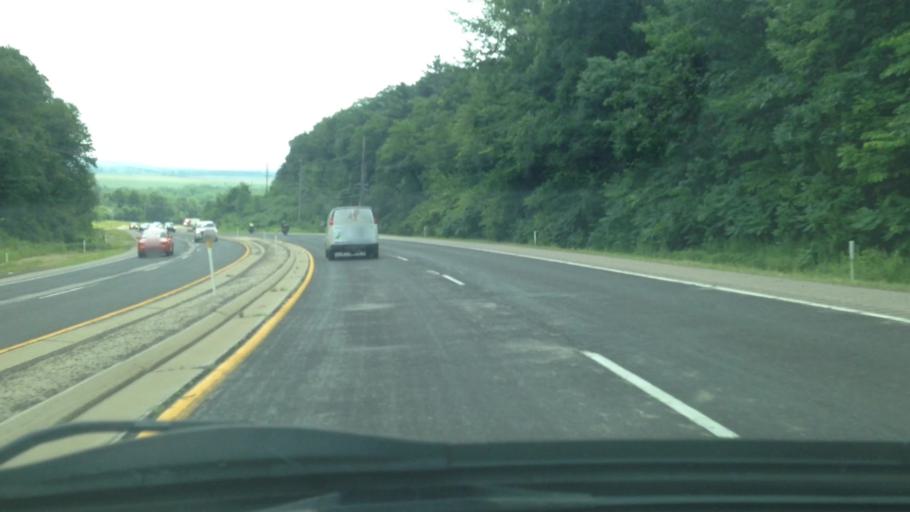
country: US
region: Wisconsin
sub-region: Sauk County
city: West Baraboo
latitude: 43.3935
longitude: -89.7716
